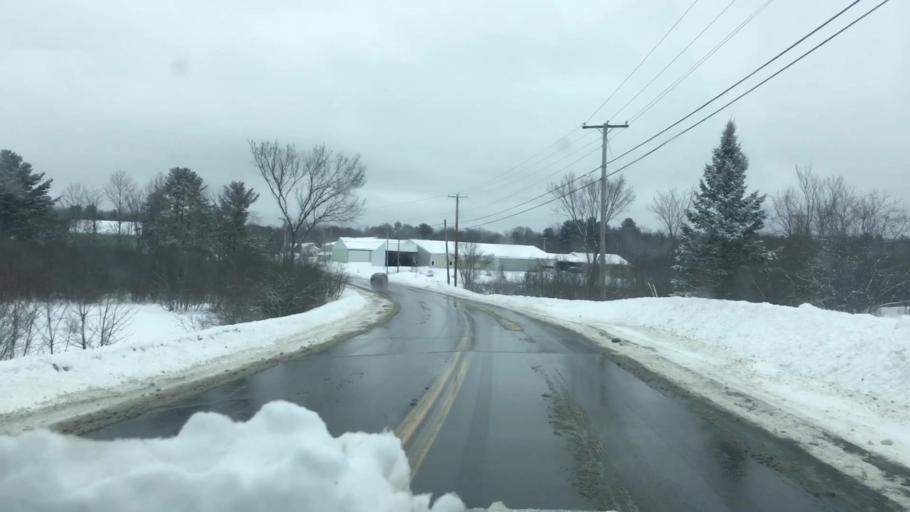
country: US
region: Maine
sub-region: Penobscot County
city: Charleston
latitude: 44.9967
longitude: -69.0380
